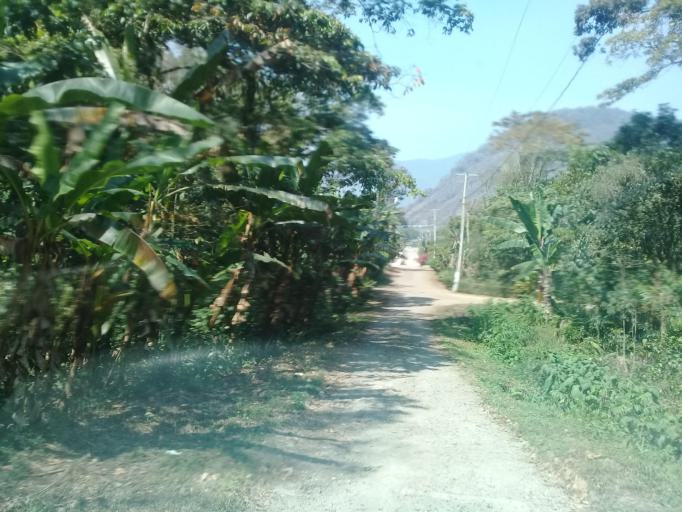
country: MX
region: Veracruz
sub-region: Ixtaczoquitlan
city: Capoluca
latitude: 18.8037
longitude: -96.9867
